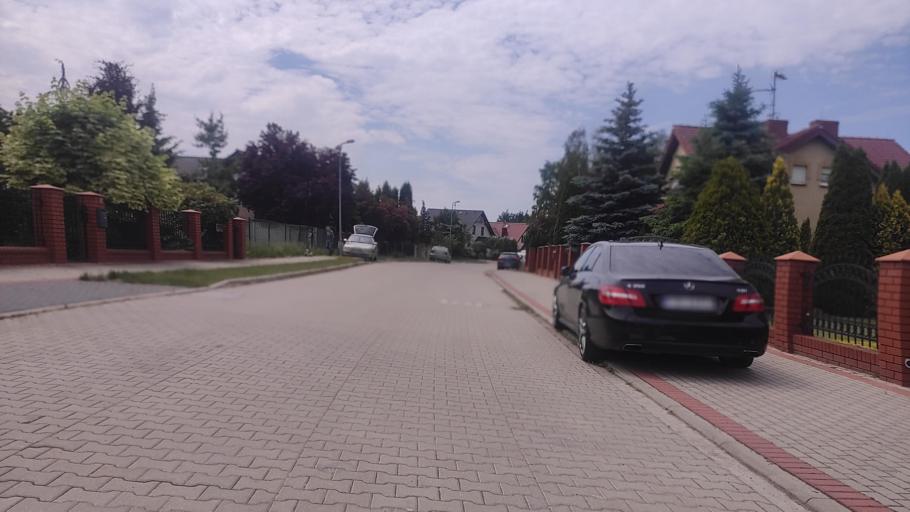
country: PL
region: Greater Poland Voivodeship
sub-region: Powiat poznanski
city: Swarzedz
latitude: 52.3968
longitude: 17.0855
